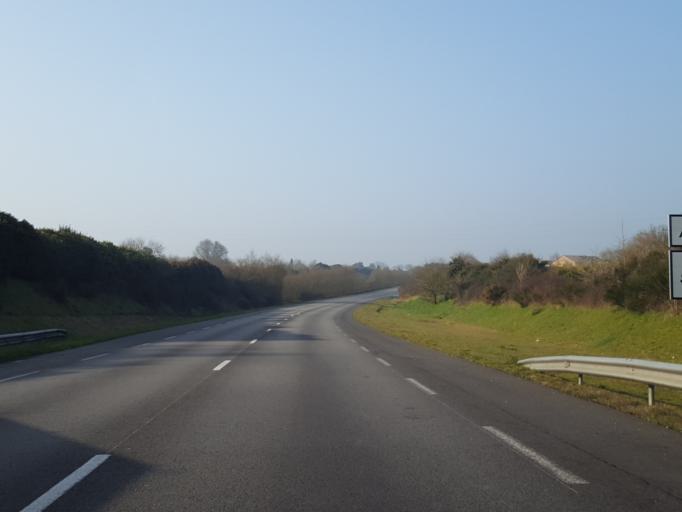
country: FR
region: Pays de la Loire
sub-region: Departement de la Vendee
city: La Roche-sur-Yon
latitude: 46.6705
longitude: -1.4591
